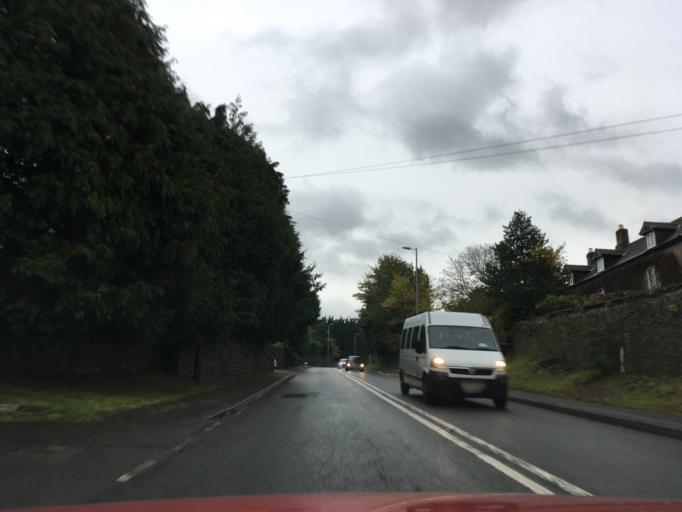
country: GB
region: Wales
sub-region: Monmouthshire
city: Chepstow
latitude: 51.6284
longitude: -2.6982
